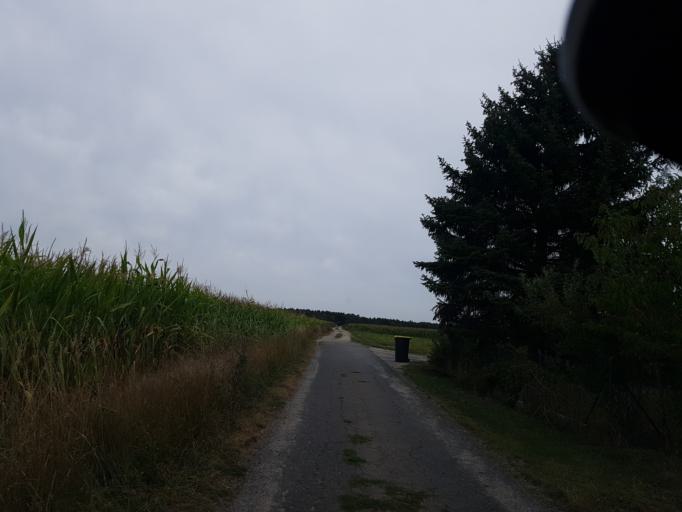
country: DE
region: Brandenburg
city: Finsterwalde
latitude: 51.6110
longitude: 13.6617
